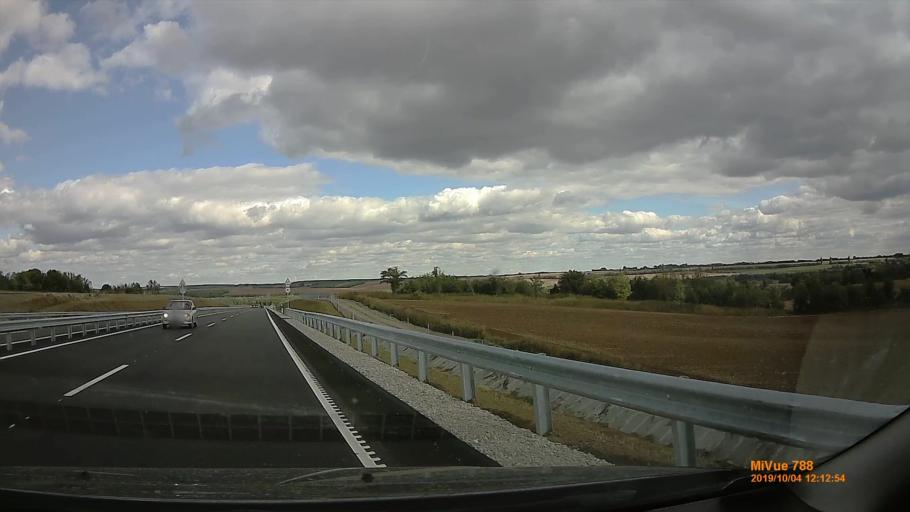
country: HU
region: Somogy
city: Kaposvar
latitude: 46.5145
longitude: 17.8121
